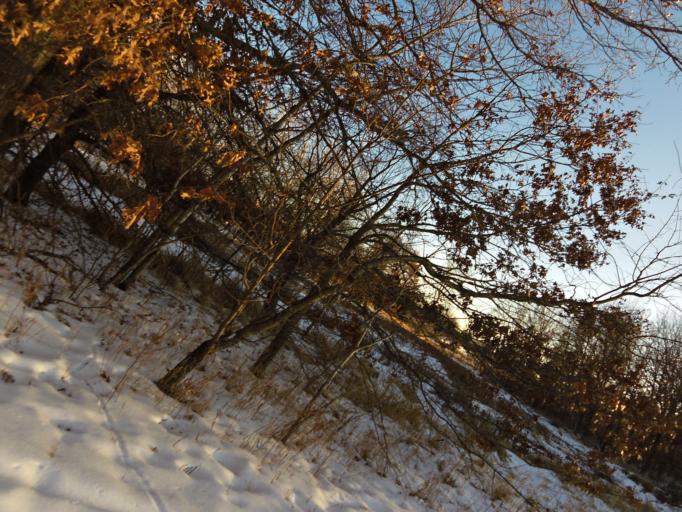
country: US
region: Minnesota
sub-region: Washington County
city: Lake Elmo
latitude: 44.9841
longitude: -92.9072
